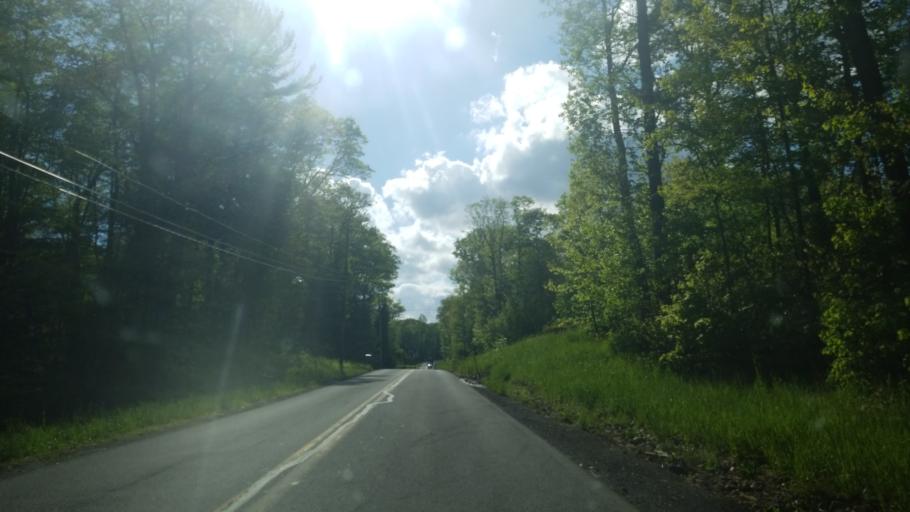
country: US
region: Pennsylvania
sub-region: Clearfield County
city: Osceola Mills
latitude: 40.9339
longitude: -78.3065
